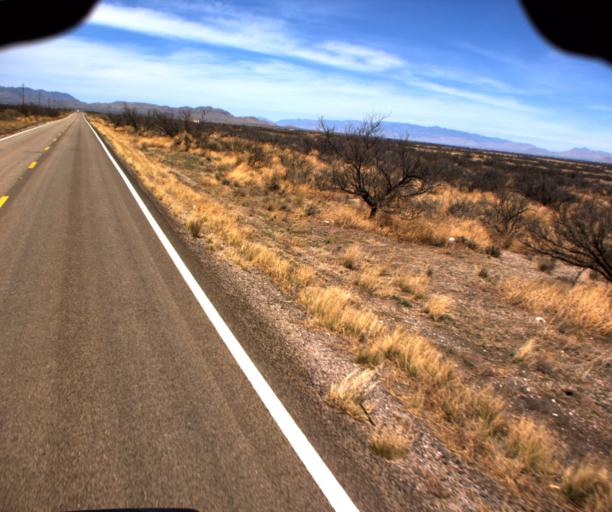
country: US
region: Arizona
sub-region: Cochise County
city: Willcox
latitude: 32.1553
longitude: -109.9387
